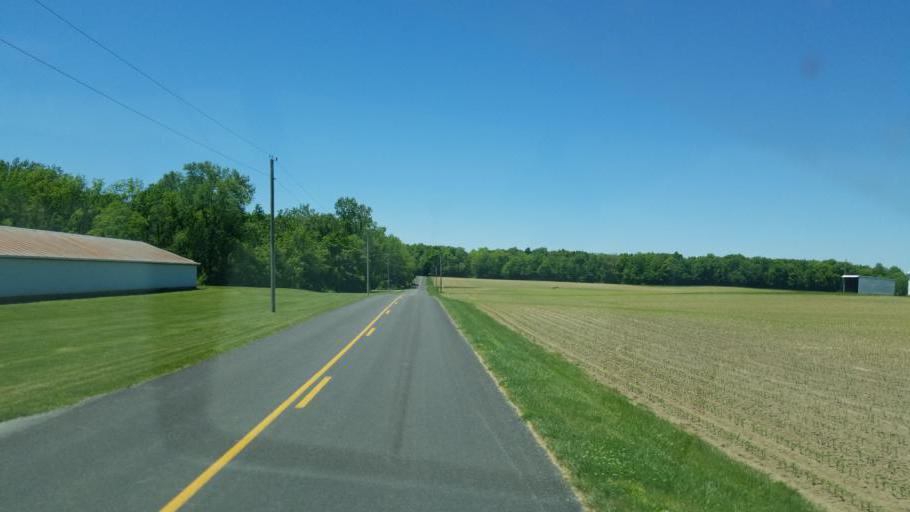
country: US
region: Ohio
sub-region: Mercer County
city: Fort Recovery
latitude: 40.3674
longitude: -84.7969
